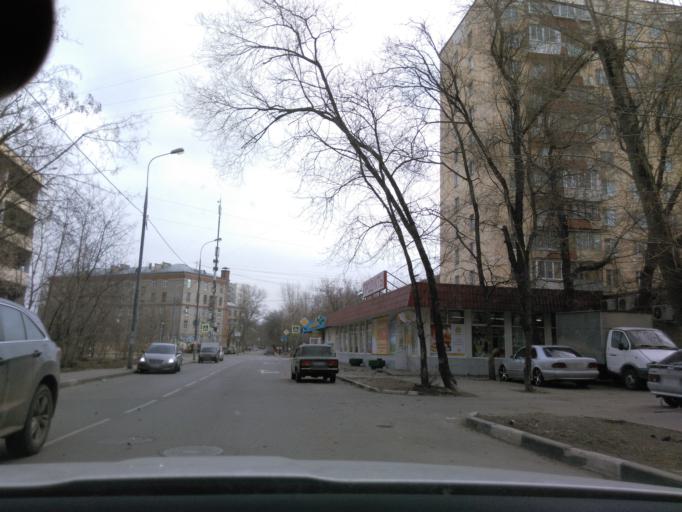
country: RU
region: Moskovskaya
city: Koptevo
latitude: 55.8276
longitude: 37.5236
